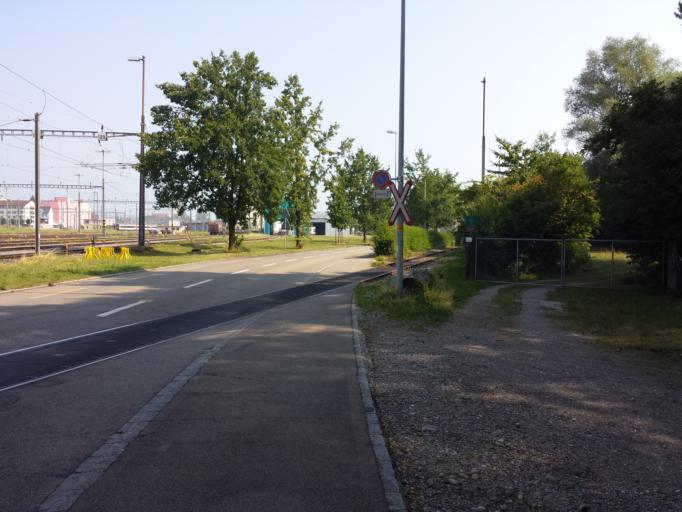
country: CH
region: Thurgau
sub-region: Arbon District
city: Romanshorn
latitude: 47.5579
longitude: 9.3789
